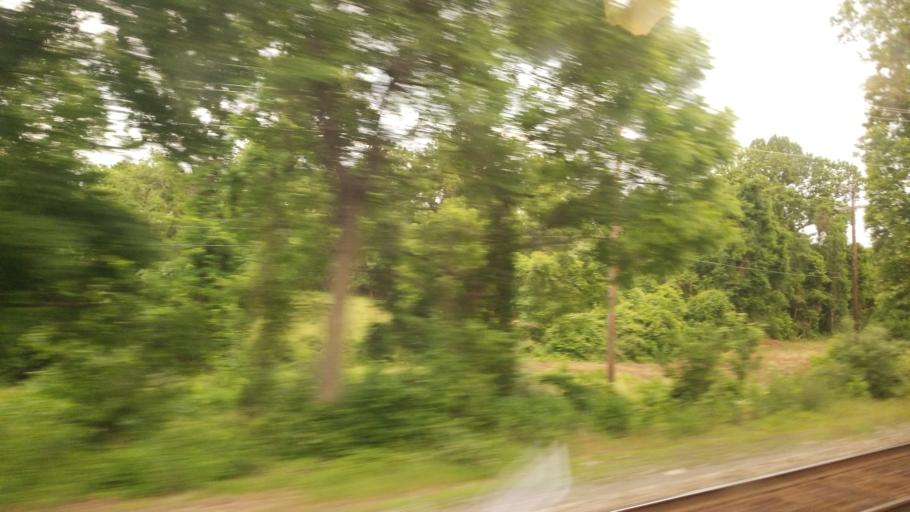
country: US
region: Virginia
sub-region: Culpeper County
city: Culpeper
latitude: 38.4644
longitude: -77.9940
